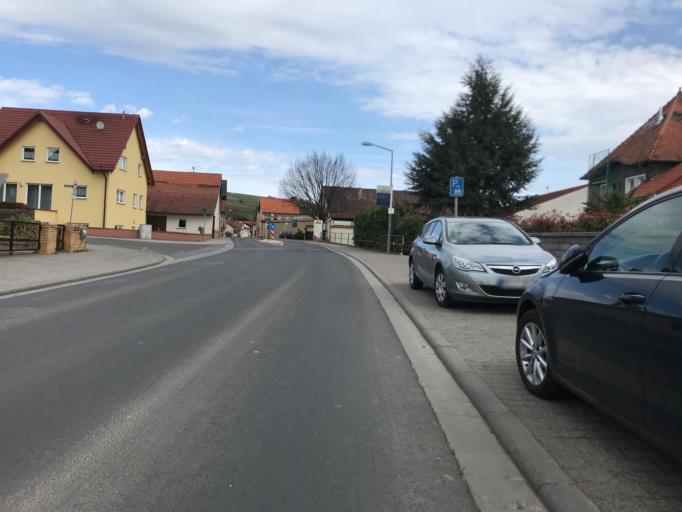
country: DE
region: Rheinland-Pfalz
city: Jugenheim
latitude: 49.8923
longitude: 8.0868
